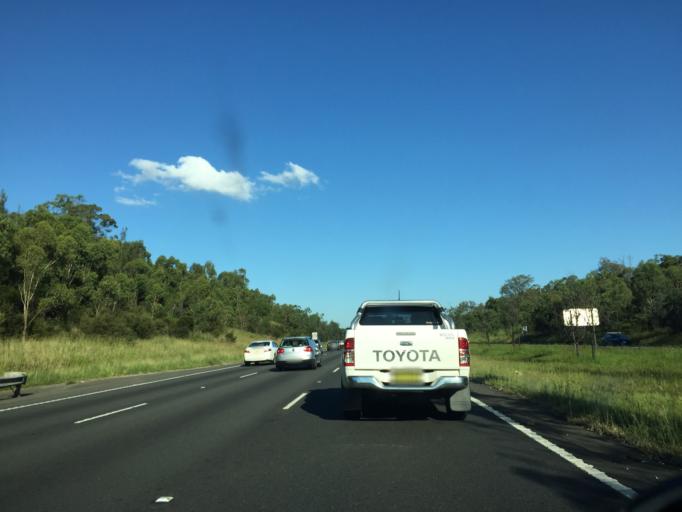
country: AU
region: New South Wales
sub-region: Blacktown
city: Mount Druitt
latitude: -33.7933
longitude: 150.8380
